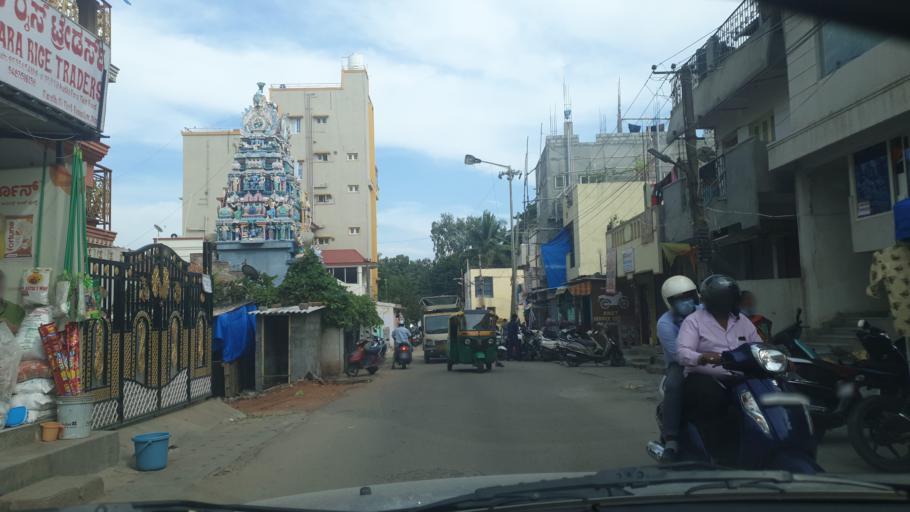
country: IN
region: Karnataka
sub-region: Bangalore Urban
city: Bangalore
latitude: 12.9647
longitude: 77.6769
